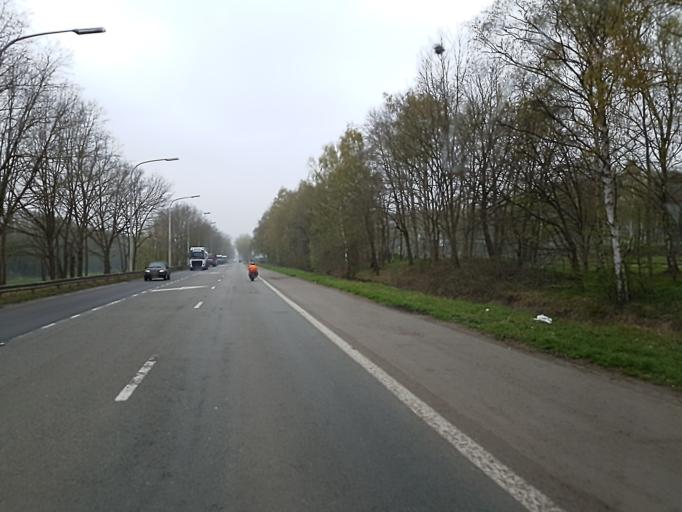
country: BE
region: Wallonia
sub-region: Province du Hainaut
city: Mons
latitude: 50.4761
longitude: 3.9306
